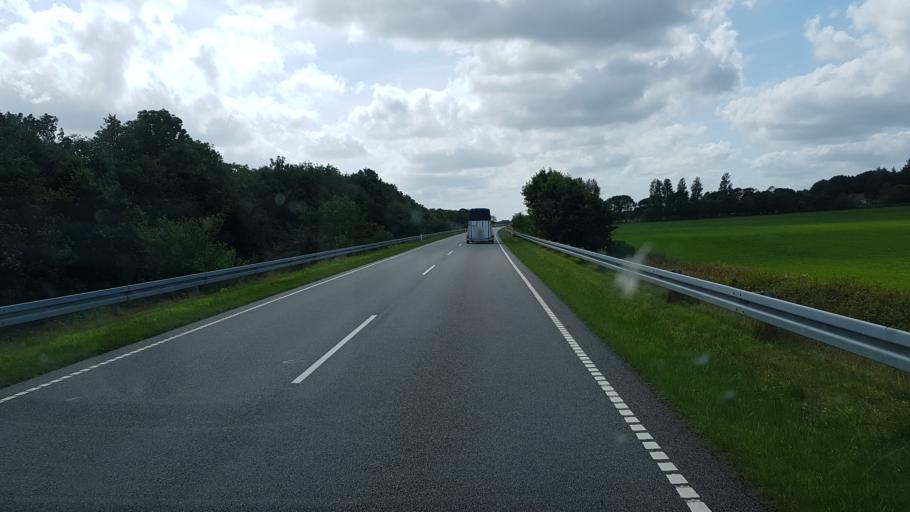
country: DK
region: South Denmark
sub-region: Vejen Kommune
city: Brorup
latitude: 55.5425
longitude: 9.0750
